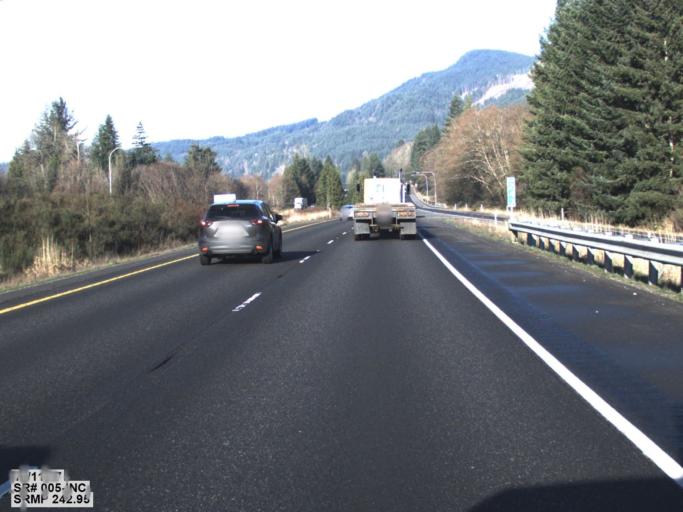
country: US
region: Washington
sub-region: Whatcom County
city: Sudden Valley
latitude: 48.6496
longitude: -122.3661
